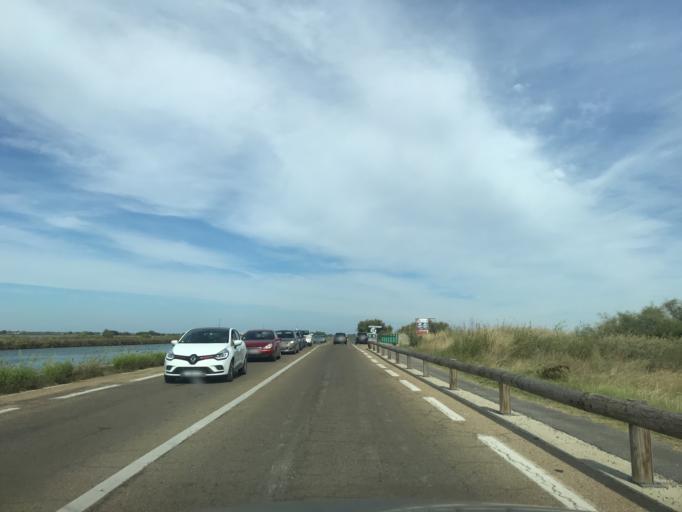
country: FR
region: Languedoc-Roussillon
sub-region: Departement du Gard
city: Le Grau-du-Roi
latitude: 43.5411
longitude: 4.1458
